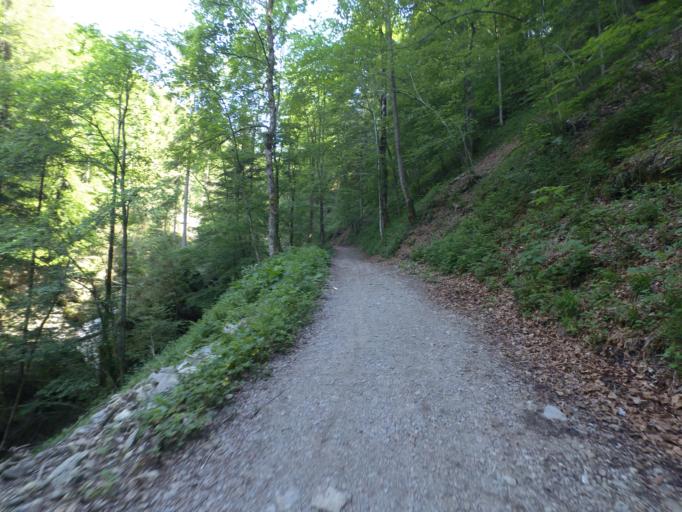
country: AT
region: Salzburg
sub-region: Politischer Bezirk Salzburg-Umgebung
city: Elsbethen
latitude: 47.7702
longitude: 13.1160
